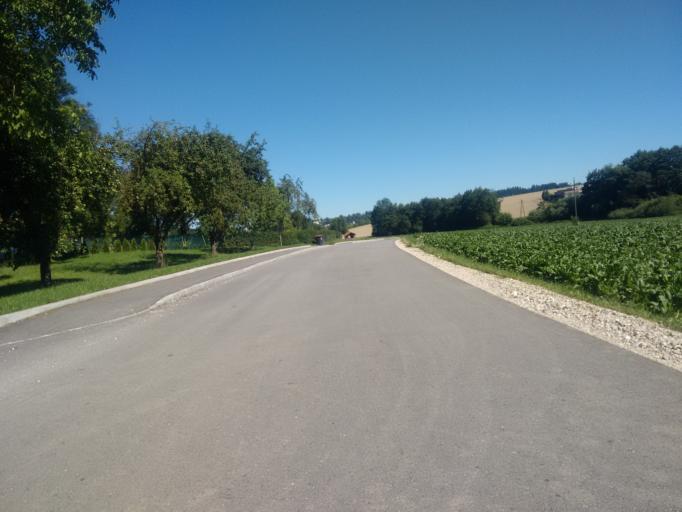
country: AT
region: Upper Austria
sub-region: Wels-Land
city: Buchkirchen
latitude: 48.2192
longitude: 14.0151
